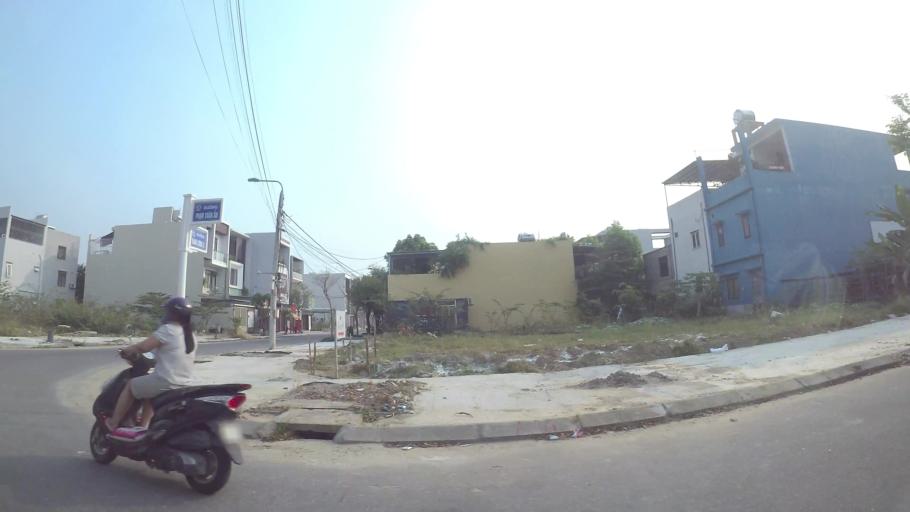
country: VN
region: Da Nang
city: Cam Le
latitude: 16.0132
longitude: 108.2196
